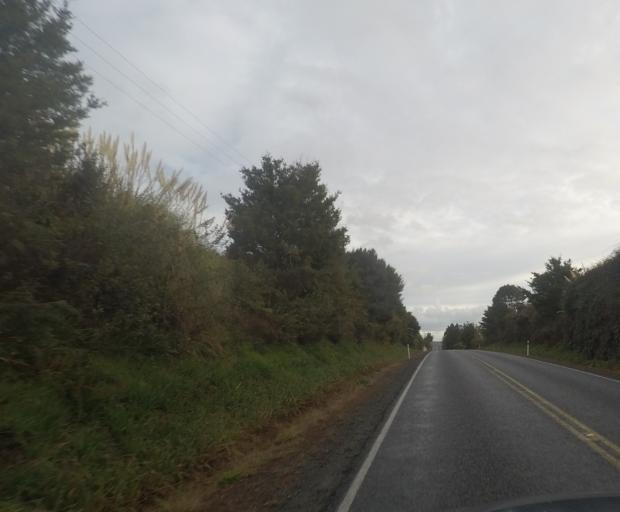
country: NZ
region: Auckland
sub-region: Auckland
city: Wellsford
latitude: -36.2101
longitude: 174.5832
